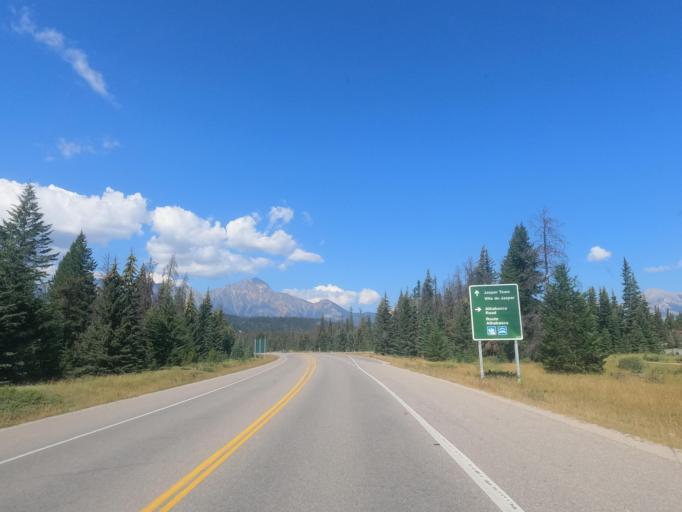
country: CA
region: Alberta
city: Jasper Park Lodge
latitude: 52.8570
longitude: -118.0786
